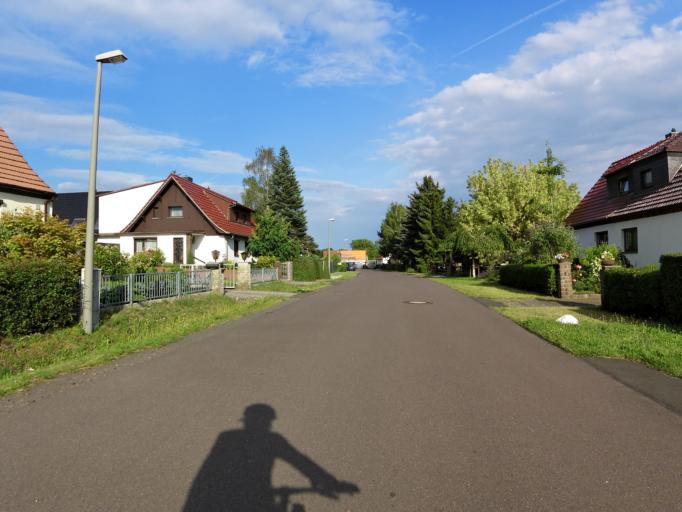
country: DE
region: Saxony
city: Zwenkau
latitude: 51.2675
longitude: 12.3017
